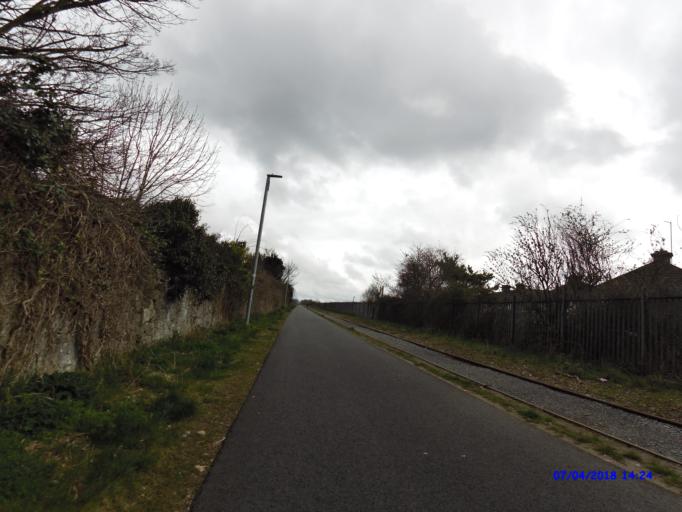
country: IE
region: Leinster
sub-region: An Iarmhi
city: Athlone
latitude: 53.4278
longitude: -7.9301
